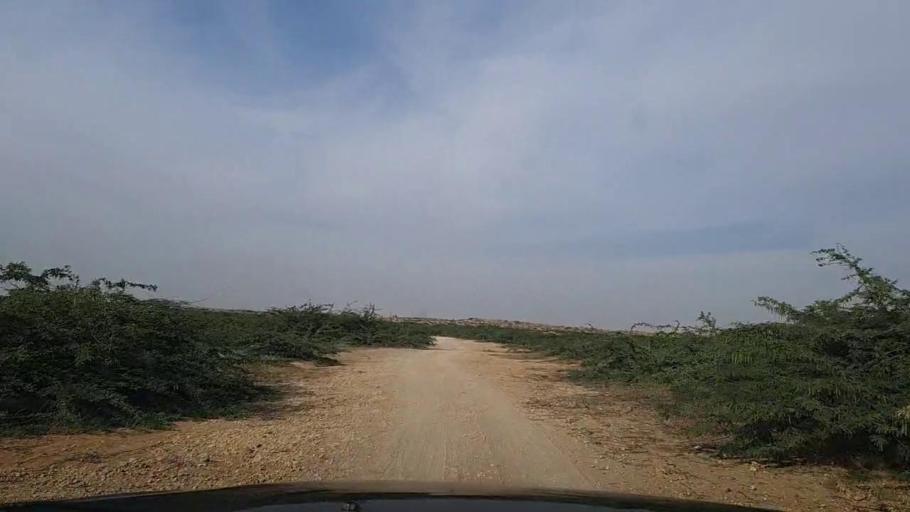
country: PK
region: Sindh
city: Gharo
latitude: 24.7814
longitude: 67.5599
